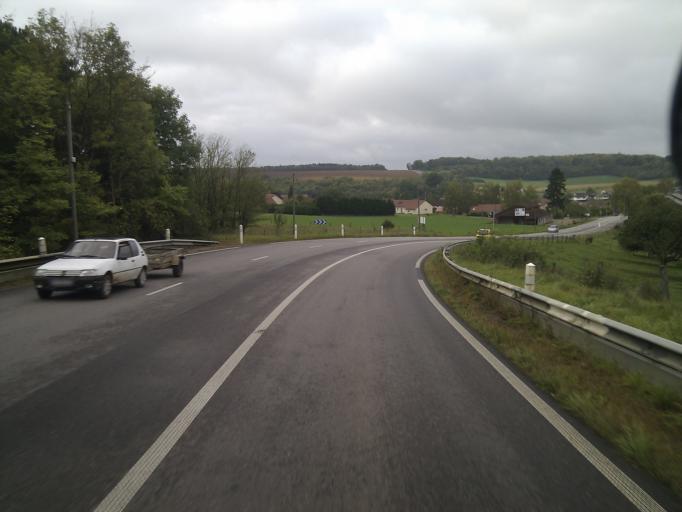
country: FR
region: Lorraine
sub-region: Departement des Vosges
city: Neufchateau
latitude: 48.4051
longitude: 5.7388
